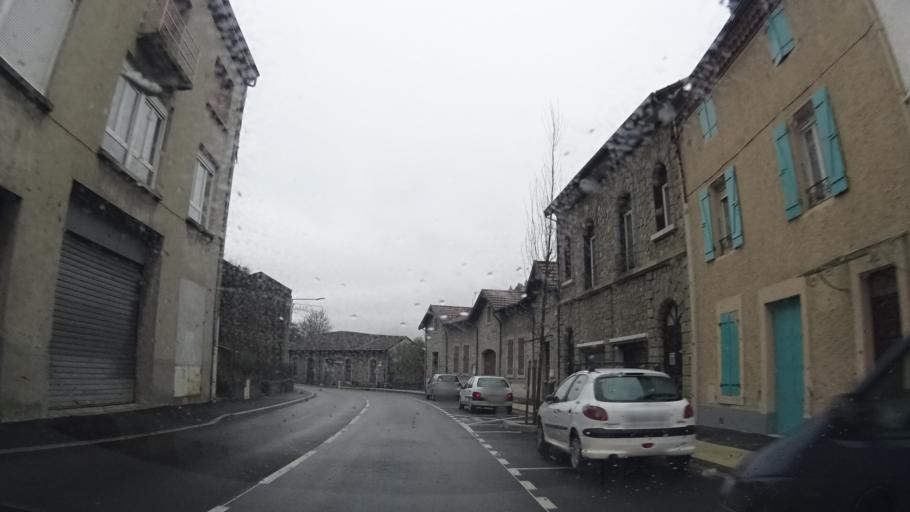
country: FR
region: Rhone-Alpes
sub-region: Departement de l'Ardeche
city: Vals-les-Bains
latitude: 44.6629
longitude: 4.3682
